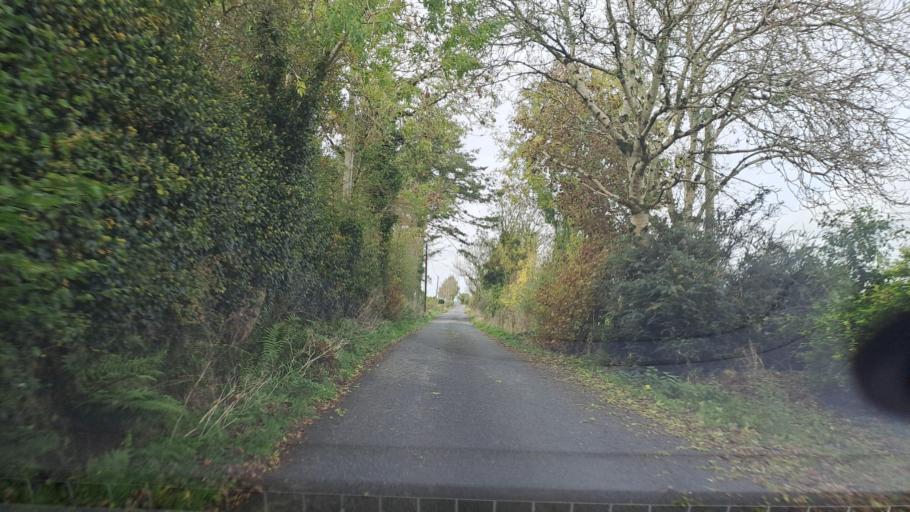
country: IE
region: Ulster
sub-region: An Cabhan
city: Kingscourt
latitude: 54.0255
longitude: -6.8324
